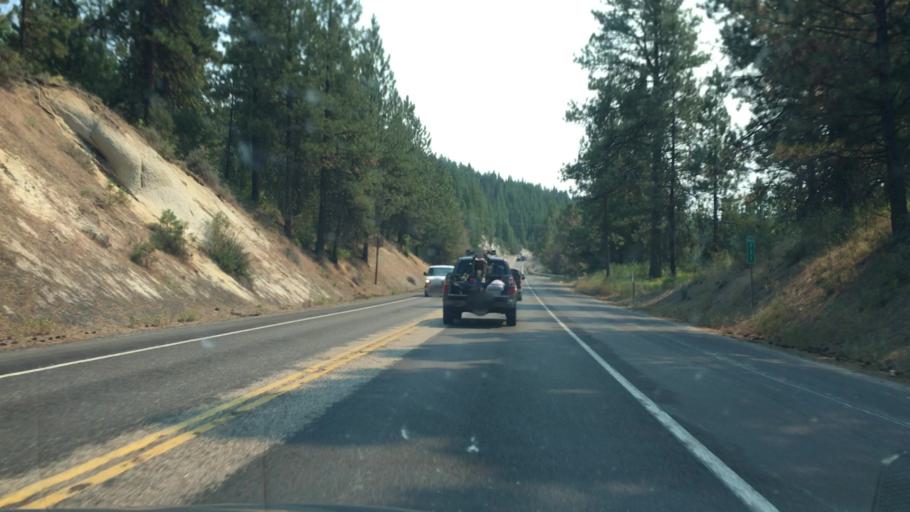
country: US
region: Idaho
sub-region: Valley County
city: Cascade
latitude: 44.5907
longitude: -116.0396
